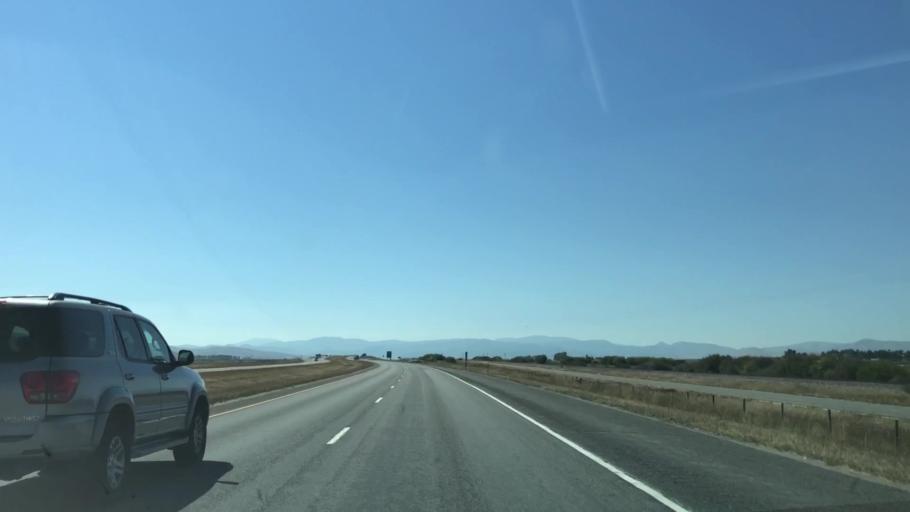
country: US
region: Montana
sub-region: Deer Lodge County
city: Warm Springs
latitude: 46.2465
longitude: -112.7625
